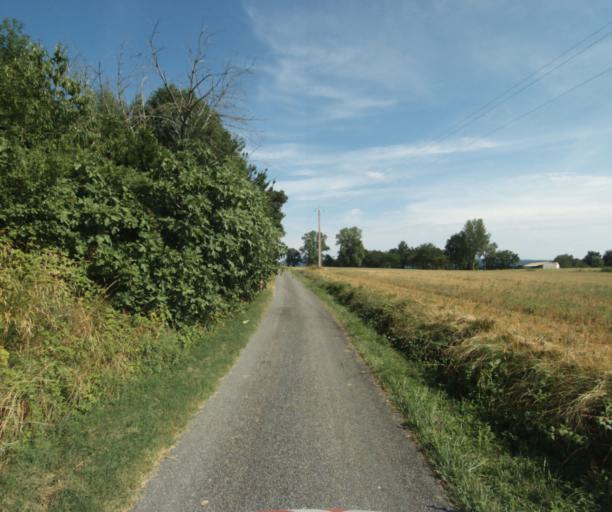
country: FR
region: Midi-Pyrenees
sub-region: Departement de la Haute-Garonne
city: Revel
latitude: 43.4972
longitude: 1.9719
